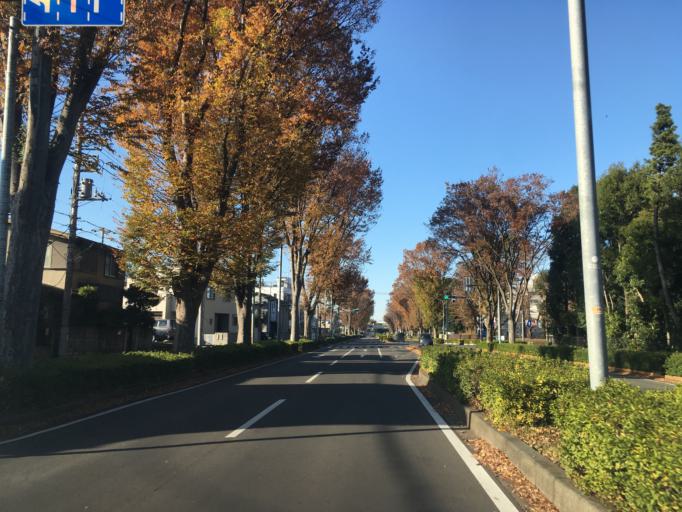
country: JP
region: Saitama
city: Tokorozawa
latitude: 35.8035
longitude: 139.4633
